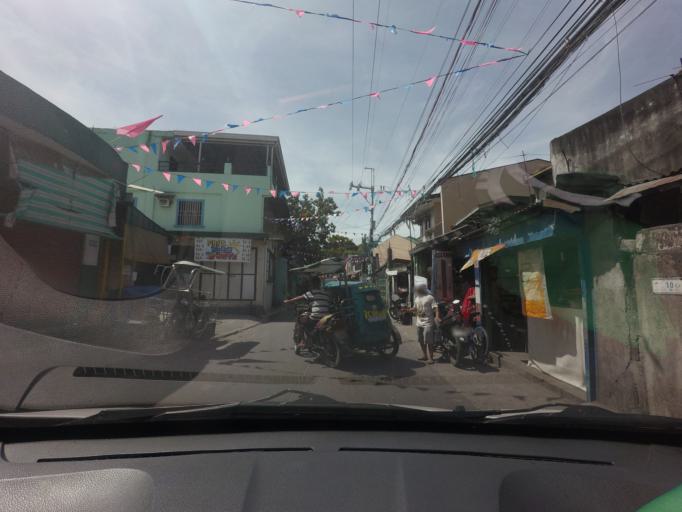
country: PH
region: Calabarzon
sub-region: Province of Rizal
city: Taguig
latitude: 14.5333
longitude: 121.0802
